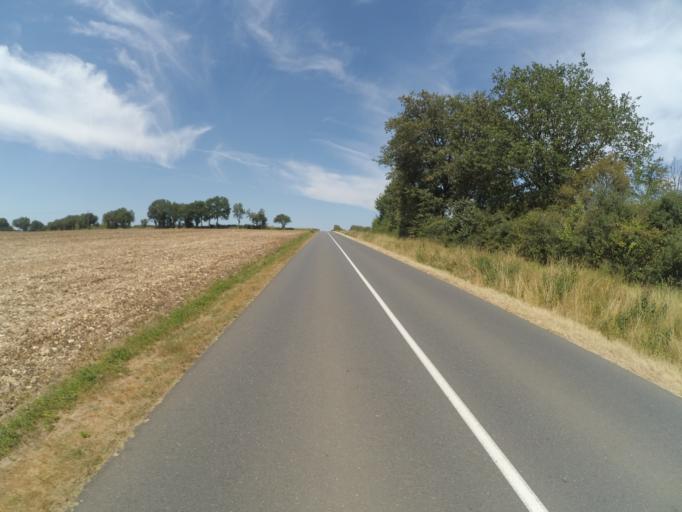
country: FR
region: Poitou-Charentes
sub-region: Departement de la Vienne
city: Usson-du-Poitou
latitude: 46.2423
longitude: 0.5254
